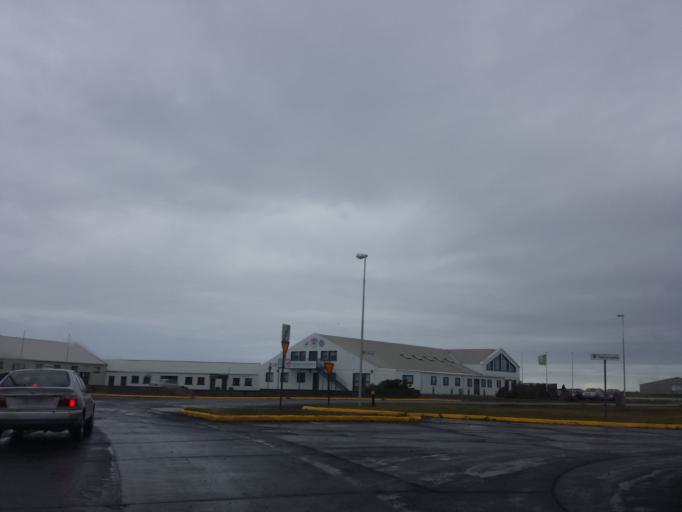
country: IS
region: Southern Peninsula
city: Sandgerdi
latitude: 64.0406
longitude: -22.7116
